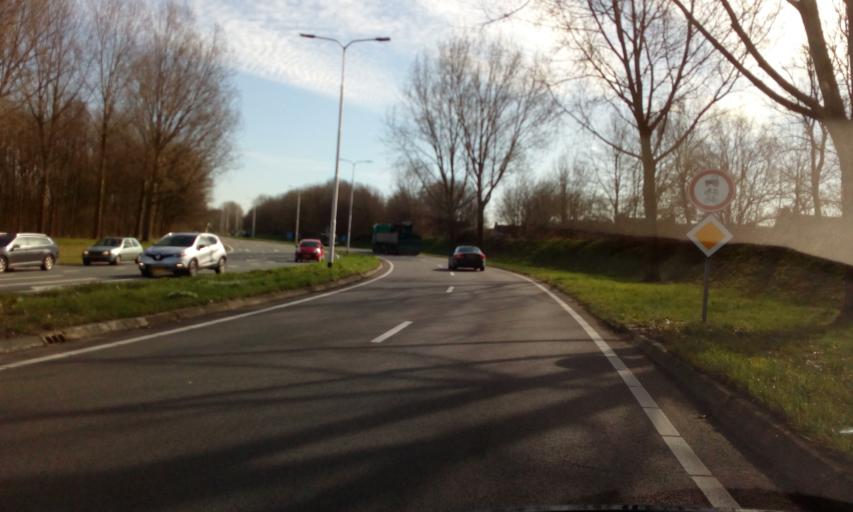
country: NL
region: South Holland
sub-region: Gemeente Alphen aan den Rijn
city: Alphen aan den Rijn
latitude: 52.1552
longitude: 4.6652
